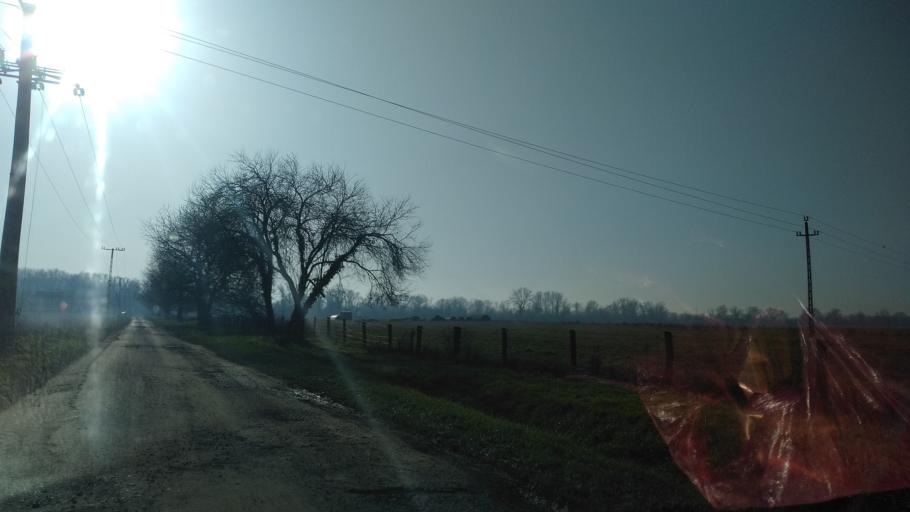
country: HU
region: Somogy
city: Barcs
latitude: 45.9514
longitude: 17.4881
